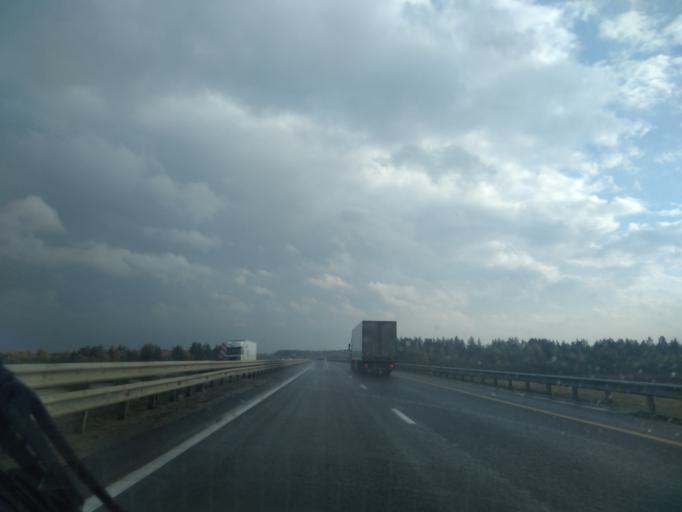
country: RU
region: Lipetsk
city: Yelets
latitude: 52.6079
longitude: 38.6658
